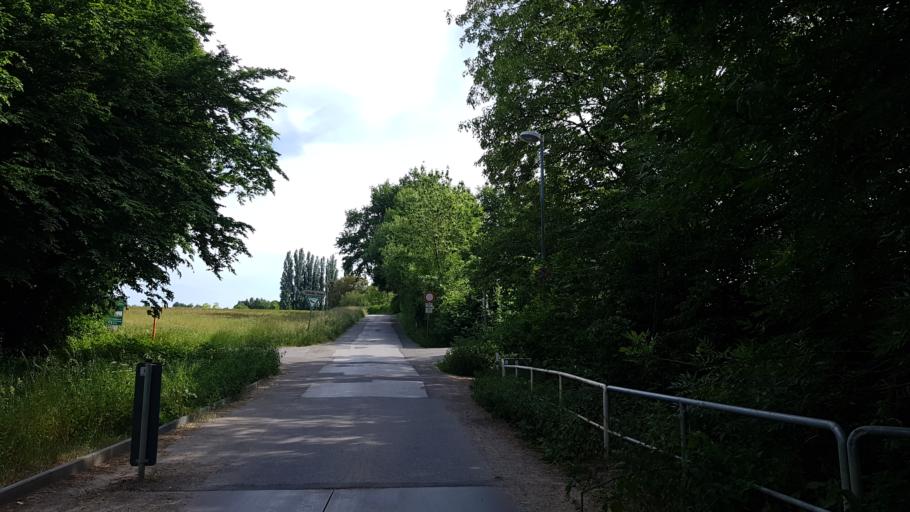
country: DE
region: North Rhine-Westphalia
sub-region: Regierungsbezirk Dusseldorf
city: Muelheim (Ruhr)
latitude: 51.4087
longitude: 6.9238
